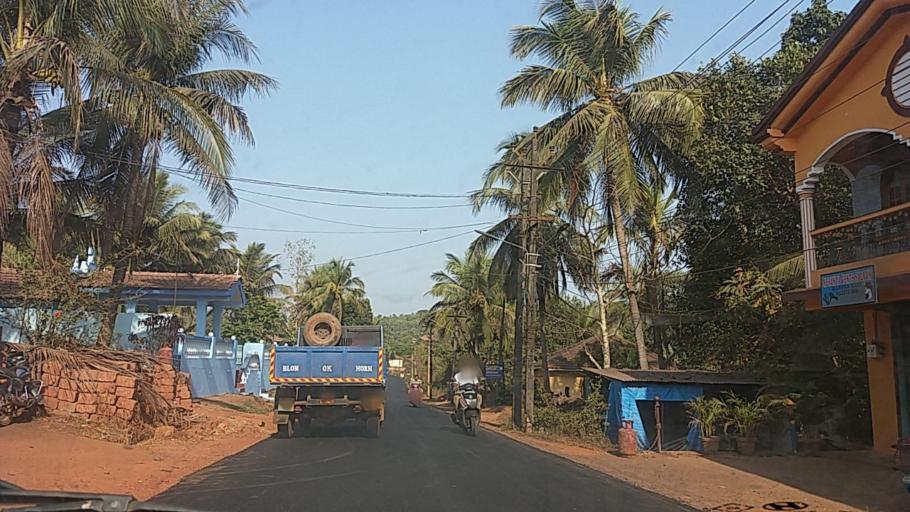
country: IN
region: Goa
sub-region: South Goa
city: Raia
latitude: 15.3072
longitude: 73.9708
